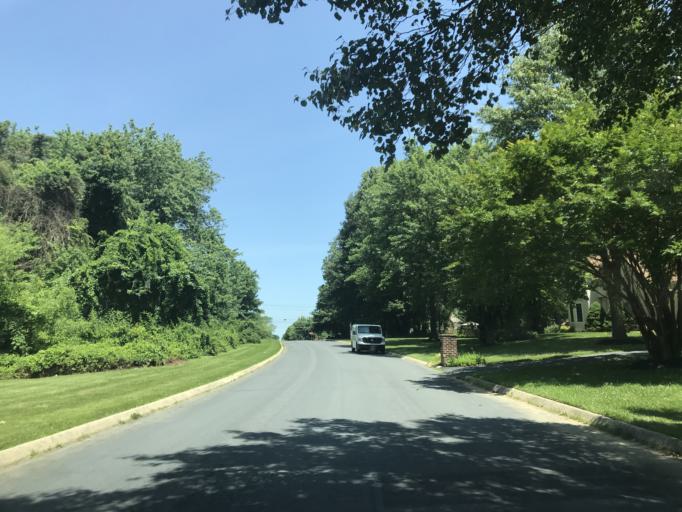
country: US
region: Maryland
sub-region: Harford County
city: South Bel Air
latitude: 39.5537
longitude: -76.2750
